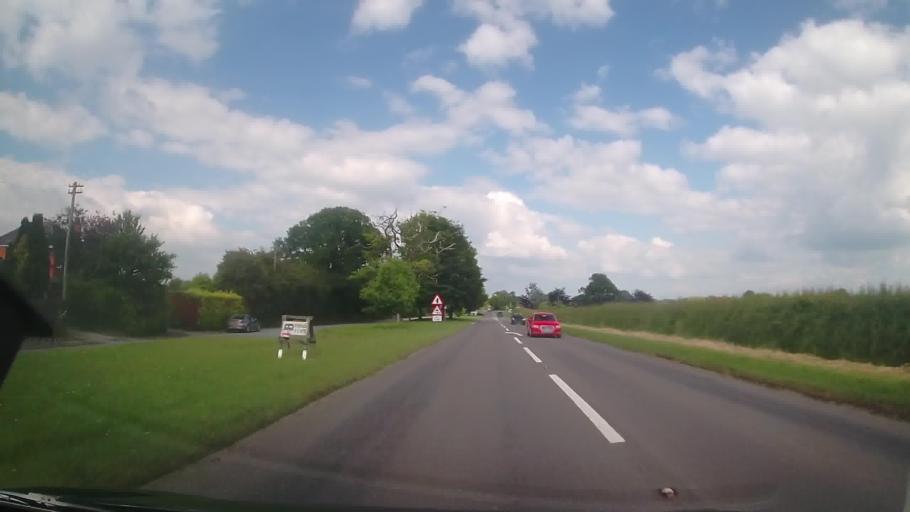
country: GB
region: England
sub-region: Shropshire
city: Whittington
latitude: 52.8715
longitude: -3.0198
